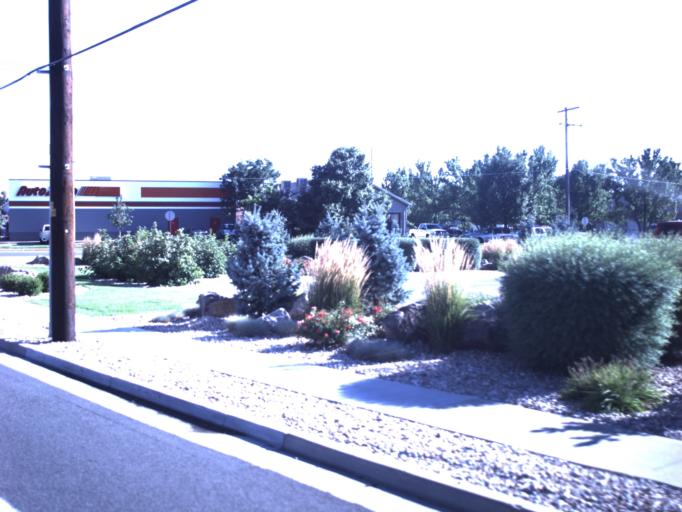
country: US
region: Utah
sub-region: Utah County
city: Orem
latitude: 40.3198
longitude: -111.7051
